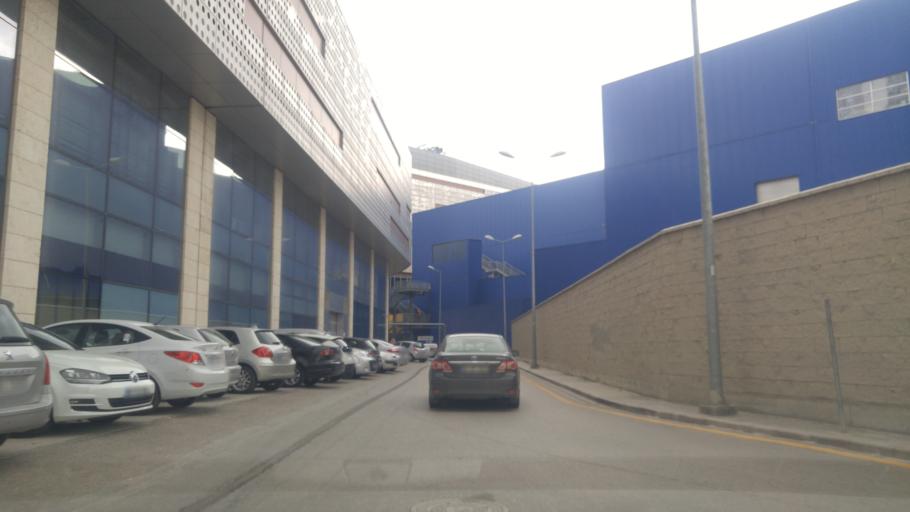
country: TR
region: Ankara
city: Mamak
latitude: 39.8894
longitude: 32.9332
